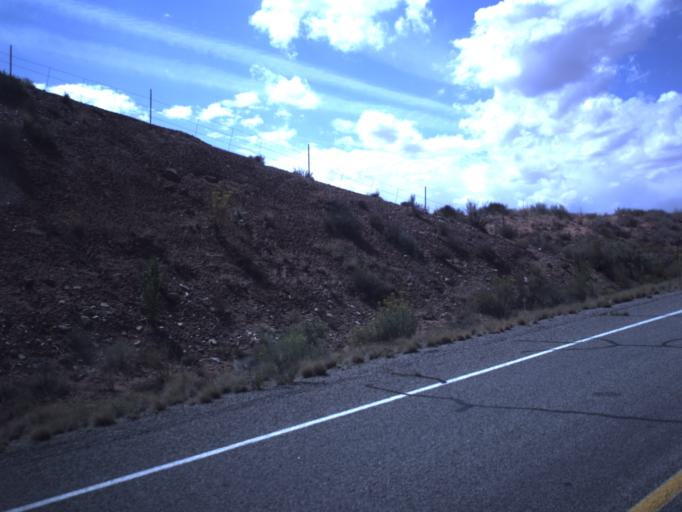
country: US
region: Utah
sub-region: San Juan County
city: Blanding
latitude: 37.2995
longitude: -109.4607
